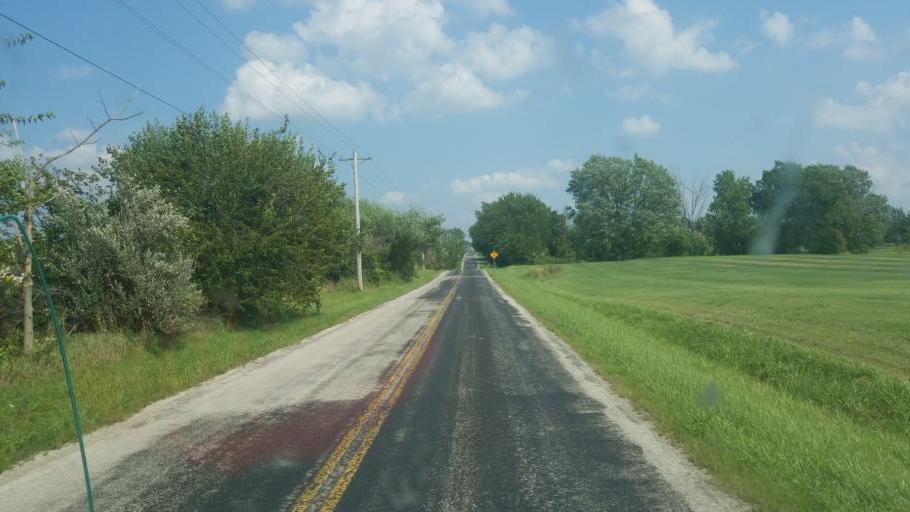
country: US
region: Ohio
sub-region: Huron County
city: New London
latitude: 41.0581
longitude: -82.3079
